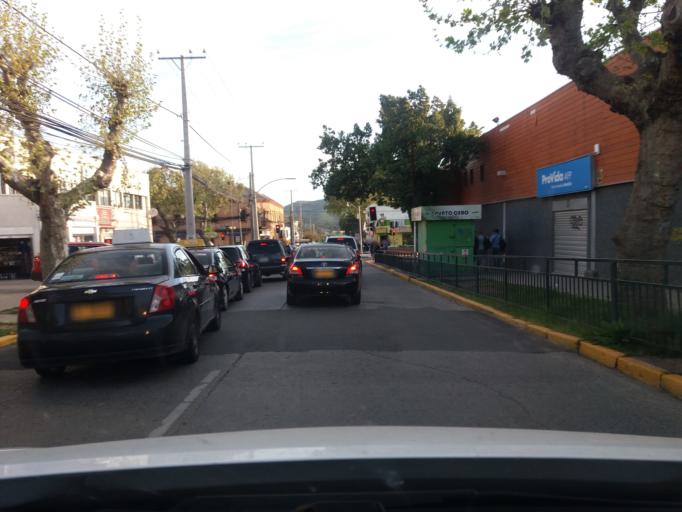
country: CL
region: Valparaiso
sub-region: Provincia de Marga Marga
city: Limache
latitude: -32.9841
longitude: -71.2767
